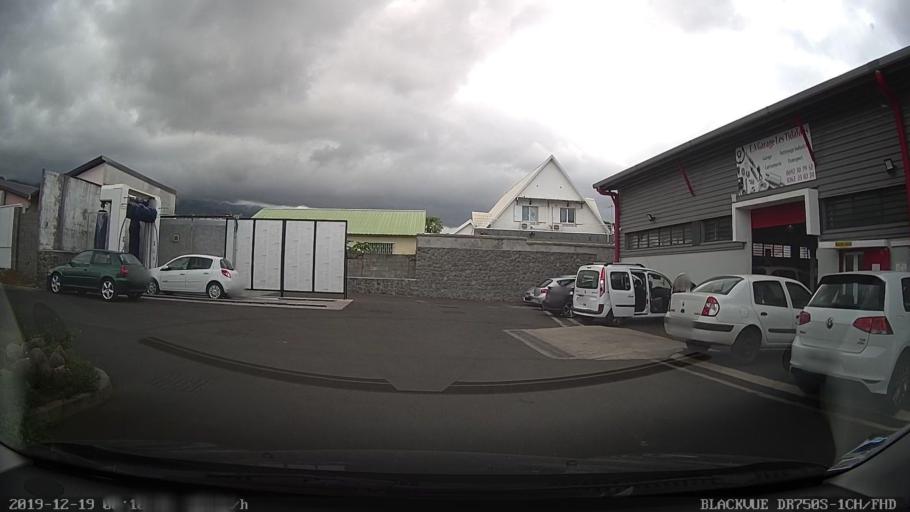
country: RE
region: Reunion
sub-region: Reunion
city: Sainte-Marie
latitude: -20.8991
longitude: 55.5034
